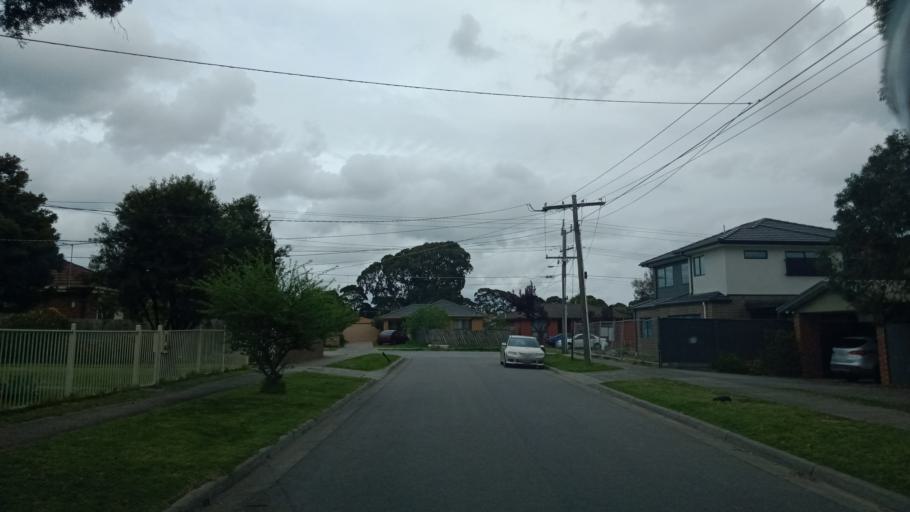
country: AU
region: Victoria
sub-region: Casey
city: Eumemmerring
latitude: -38.0000
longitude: 145.2450
